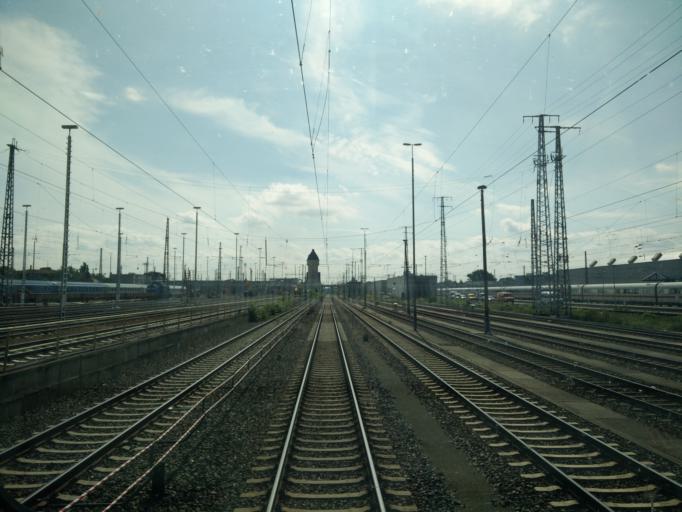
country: DE
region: Berlin
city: Rummelsburg
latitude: 52.4907
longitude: 13.5036
